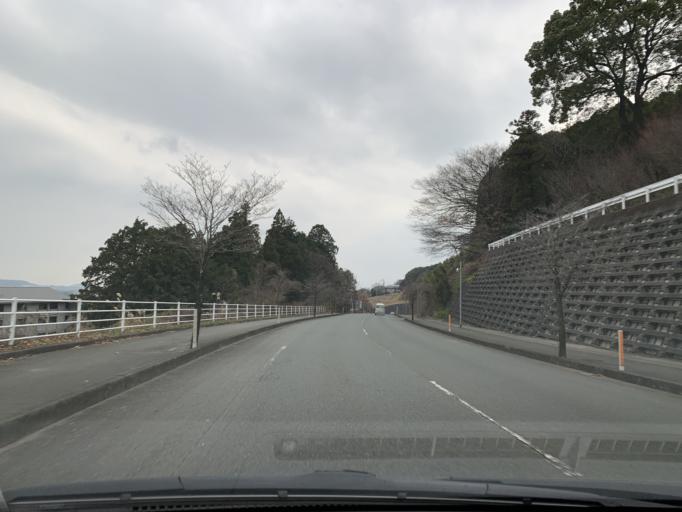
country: JP
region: Kumamoto
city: Ozu
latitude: 32.8825
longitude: 130.8808
